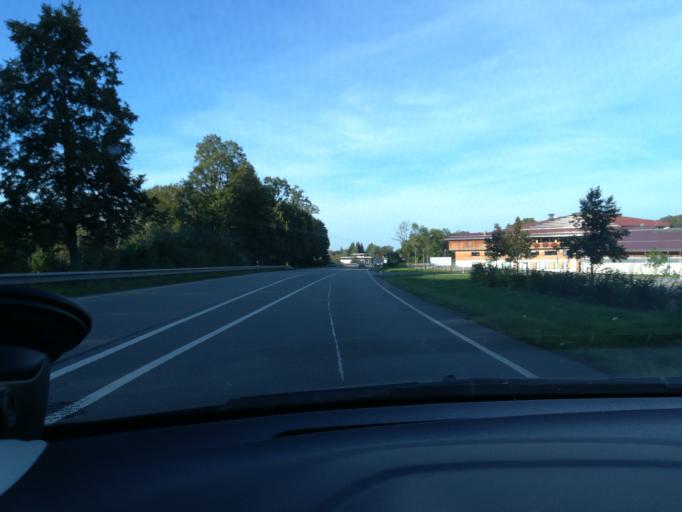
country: DE
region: Bavaria
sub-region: Upper Bavaria
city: Miesbach
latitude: 47.7791
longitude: 11.8294
